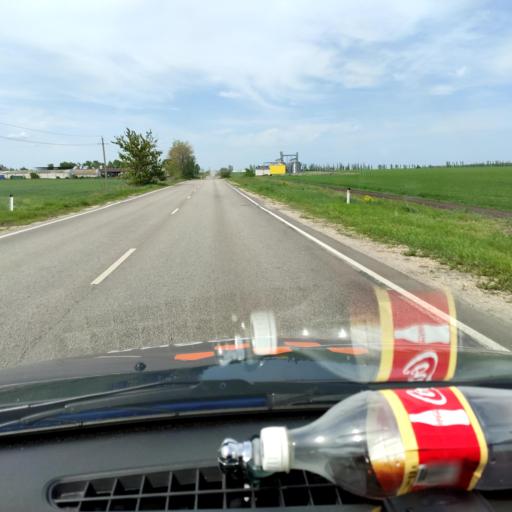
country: RU
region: Voronezj
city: Novaya Usman'
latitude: 51.5757
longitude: 39.3752
